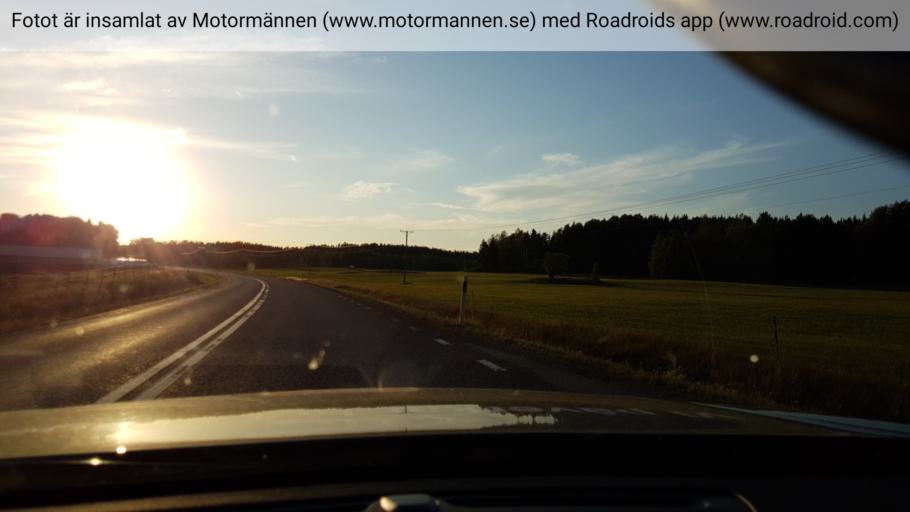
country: SE
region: OErebro
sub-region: Karlskoga Kommun
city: Karlskoga
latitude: 59.3908
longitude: 14.4682
